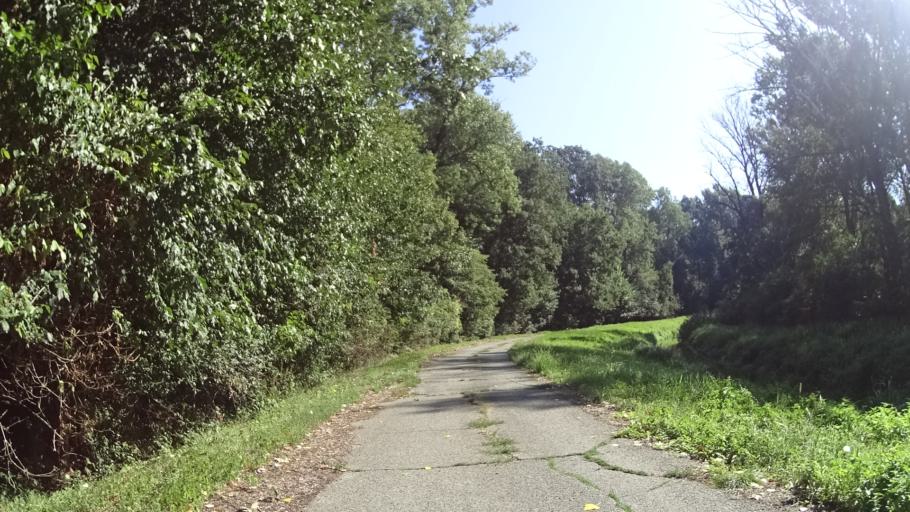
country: CZ
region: South Moravian
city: Hodonin
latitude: 48.8195
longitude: 17.1328
